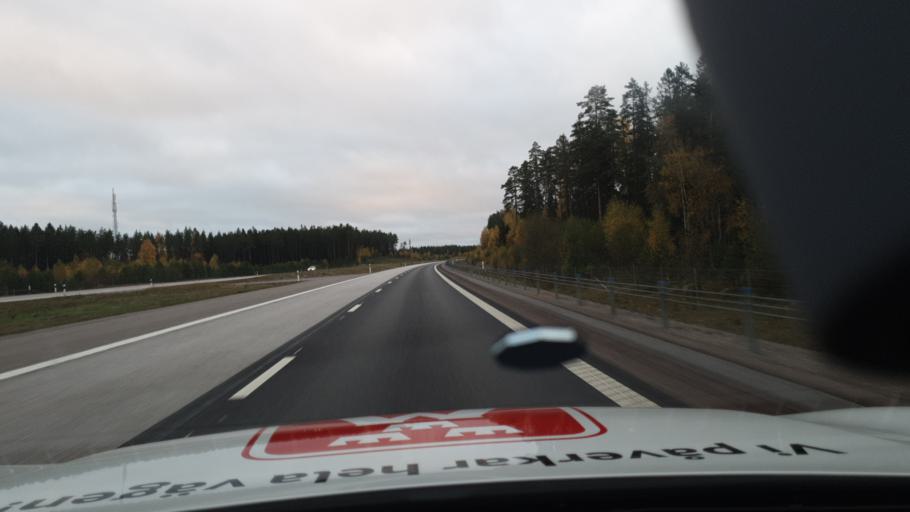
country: SE
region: Uppsala
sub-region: Tierps Kommun
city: Tierp
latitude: 60.2757
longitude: 17.5015
